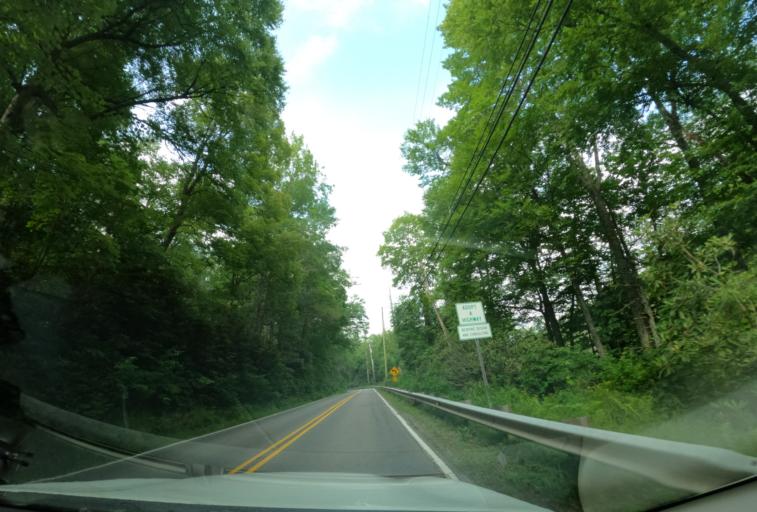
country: US
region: North Carolina
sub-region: Macon County
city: Franklin
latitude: 35.0681
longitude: -83.1887
